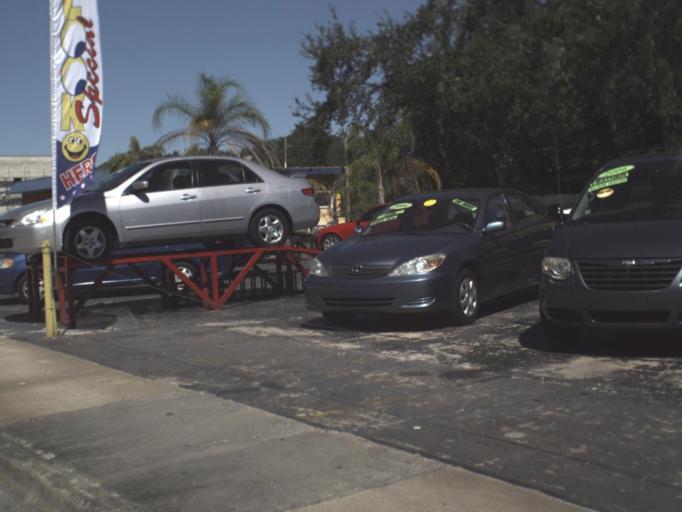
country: US
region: Florida
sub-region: Lee County
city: Fort Myers
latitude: 26.6264
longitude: -81.8722
